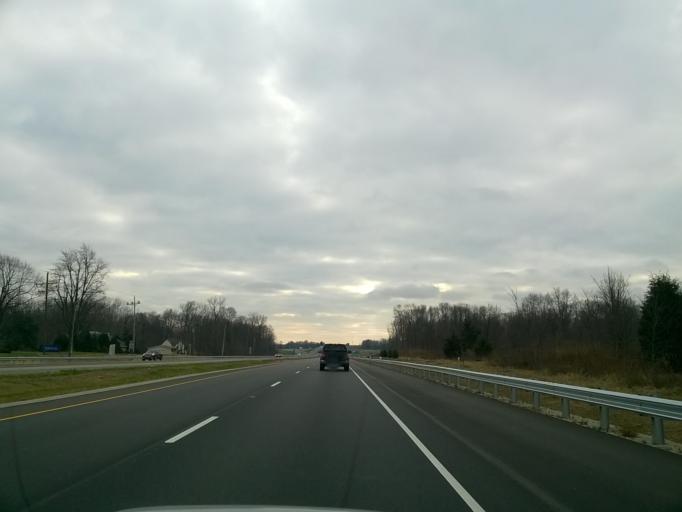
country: US
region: Indiana
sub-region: Hamilton County
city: Westfield
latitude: 40.0732
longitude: -86.1281
